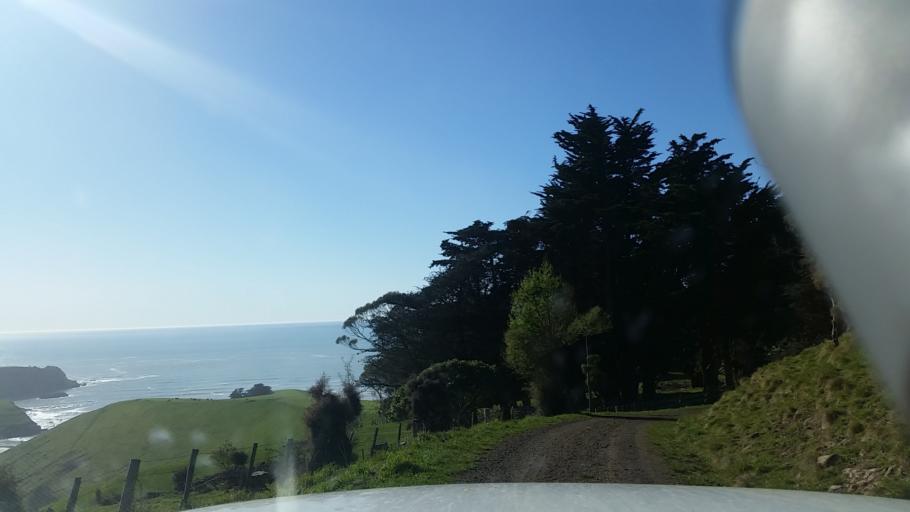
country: NZ
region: Canterbury
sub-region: Christchurch City
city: Christchurch
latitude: -43.6690
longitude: 173.0261
